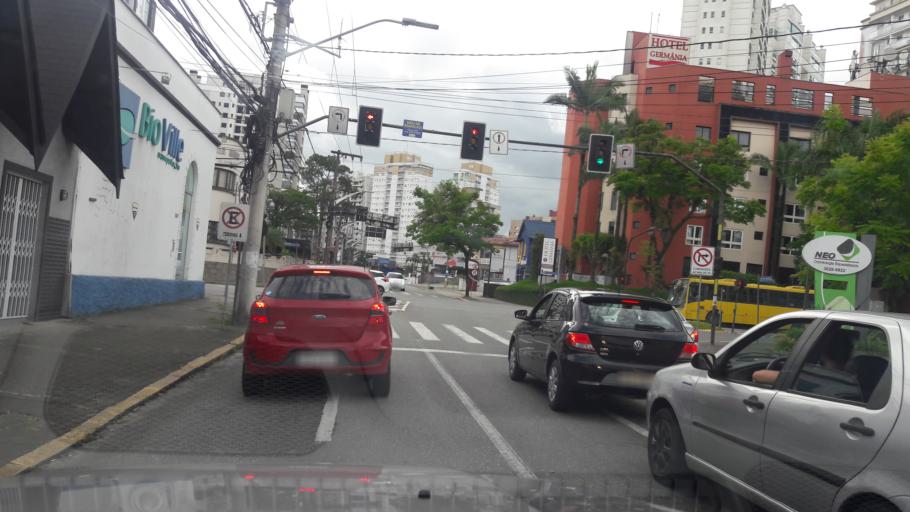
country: BR
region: Santa Catarina
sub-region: Joinville
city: Joinville
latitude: -26.3073
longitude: -48.8453
